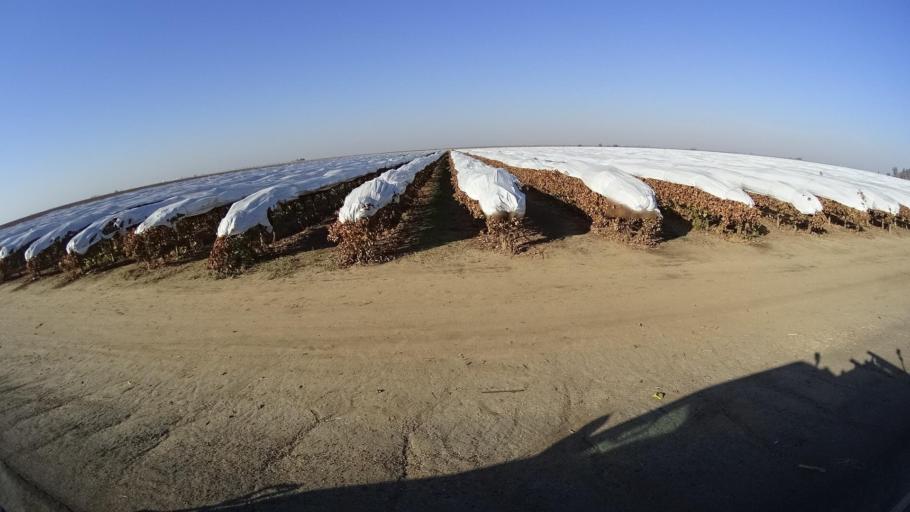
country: US
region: California
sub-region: Kern County
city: McFarland
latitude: 35.7333
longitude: -119.1694
